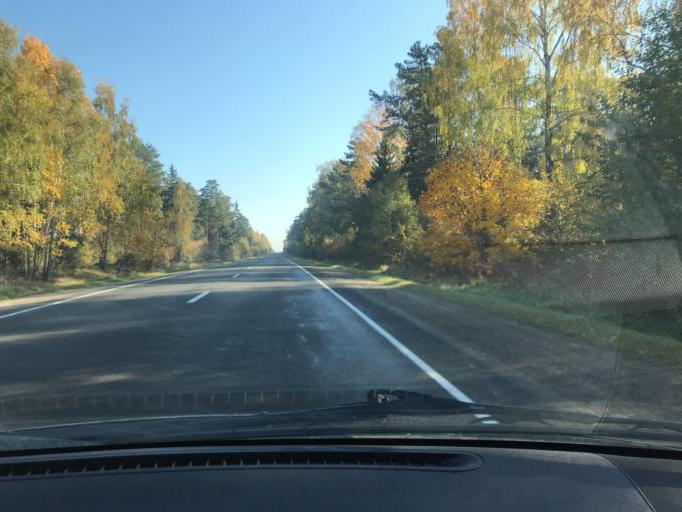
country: BY
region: Brest
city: Lyakhavichy
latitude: 52.9594
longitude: 26.3794
